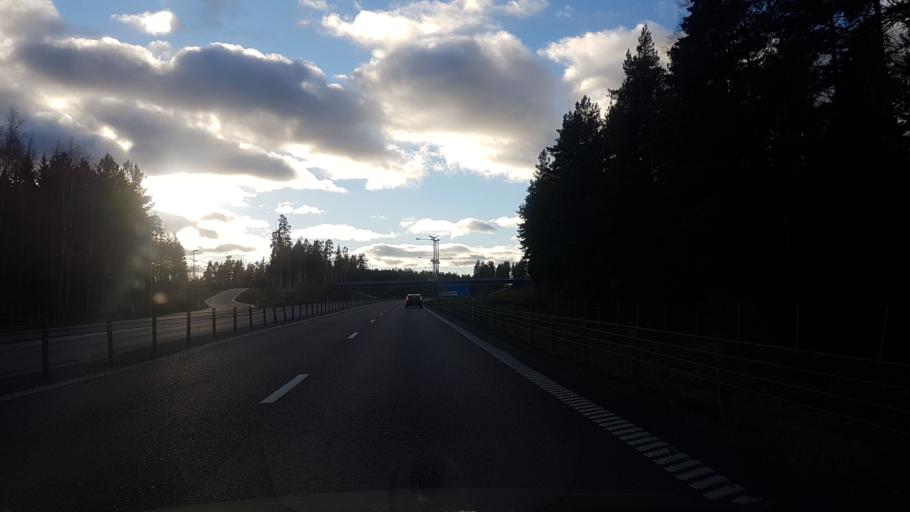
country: SE
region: Gaevleborg
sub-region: Sandvikens Kommun
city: Sandviken
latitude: 60.6248
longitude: 16.7344
